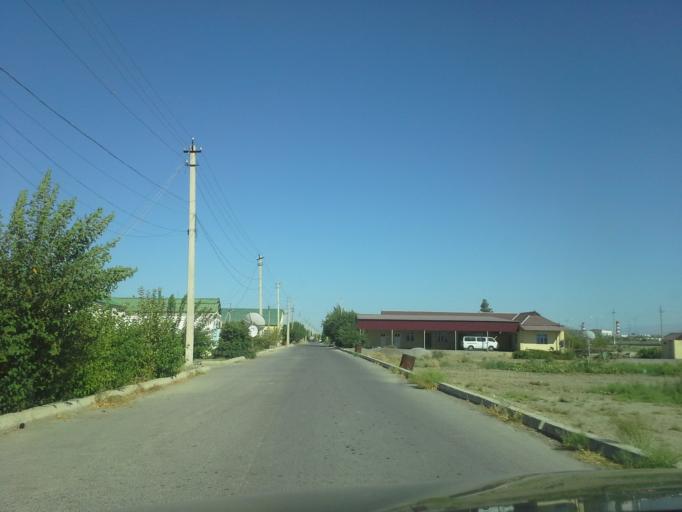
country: TM
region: Ahal
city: Abadan
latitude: 38.0731
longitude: 58.1503
